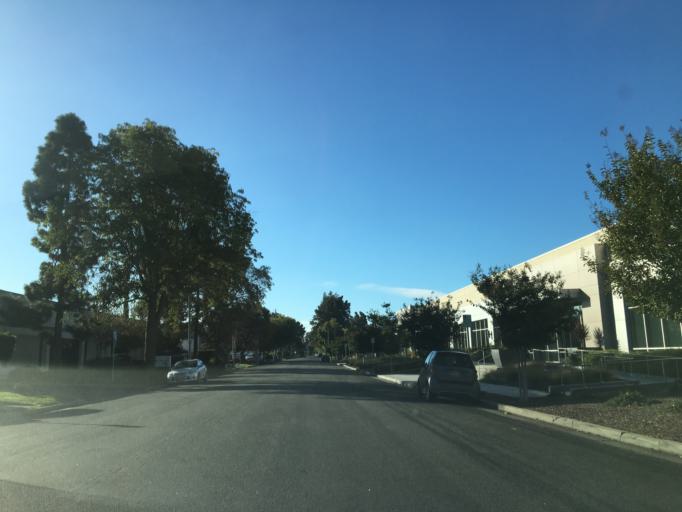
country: US
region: California
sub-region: Santa Clara County
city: Sunnyvale
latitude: 37.4093
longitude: -121.9905
